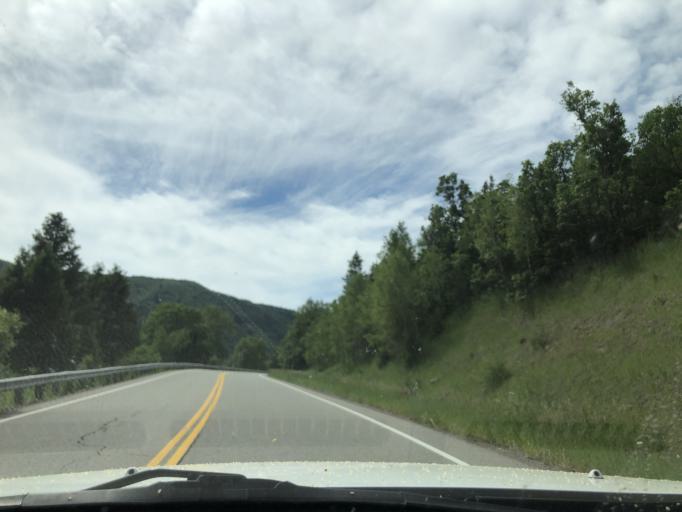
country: US
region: Colorado
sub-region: Delta County
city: Paonia
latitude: 38.9778
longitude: -107.3441
